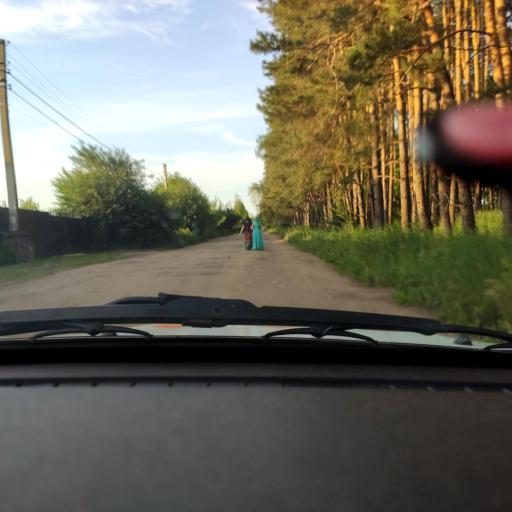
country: RU
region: Voronezj
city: Podgornoye
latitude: 51.8350
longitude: 39.1975
